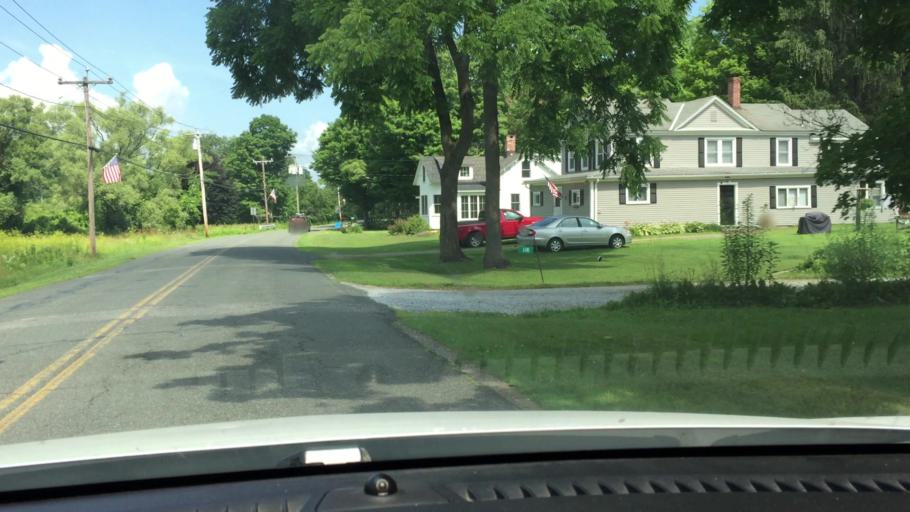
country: US
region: Massachusetts
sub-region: Berkshire County
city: Lee
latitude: 42.2472
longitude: -73.2054
